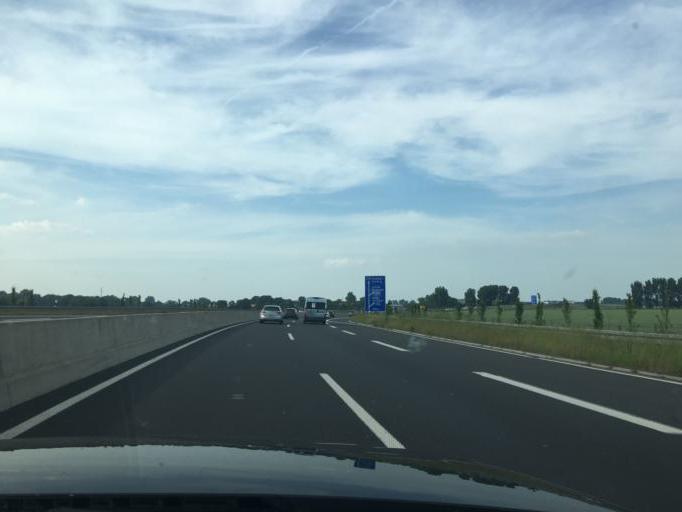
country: DE
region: North Rhine-Westphalia
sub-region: Regierungsbezirk Dusseldorf
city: Hochfeld
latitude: 51.3414
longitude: 6.7510
